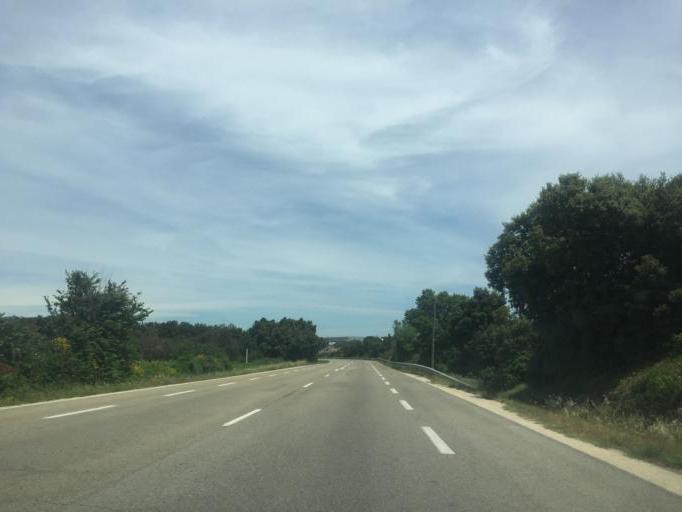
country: FR
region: Languedoc-Roussillon
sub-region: Departement du Gard
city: Pujaut
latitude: 44.0148
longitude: 4.7387
